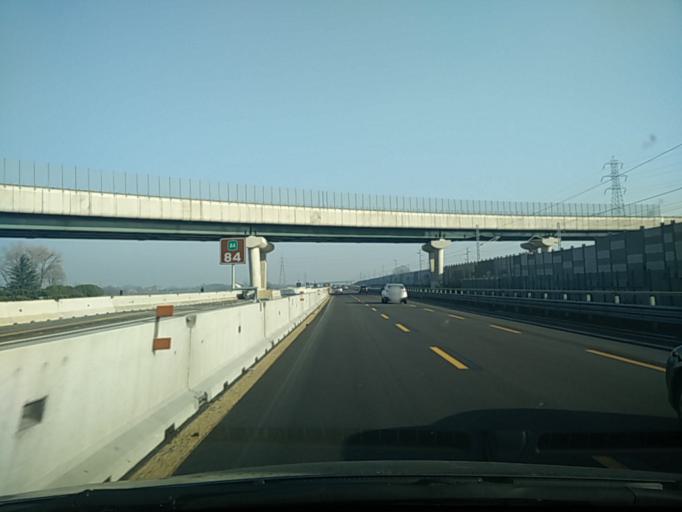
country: IT
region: Lombardy
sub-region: Citta metropolitana di Milano
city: Casone
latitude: 45.4923
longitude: 8.8780
